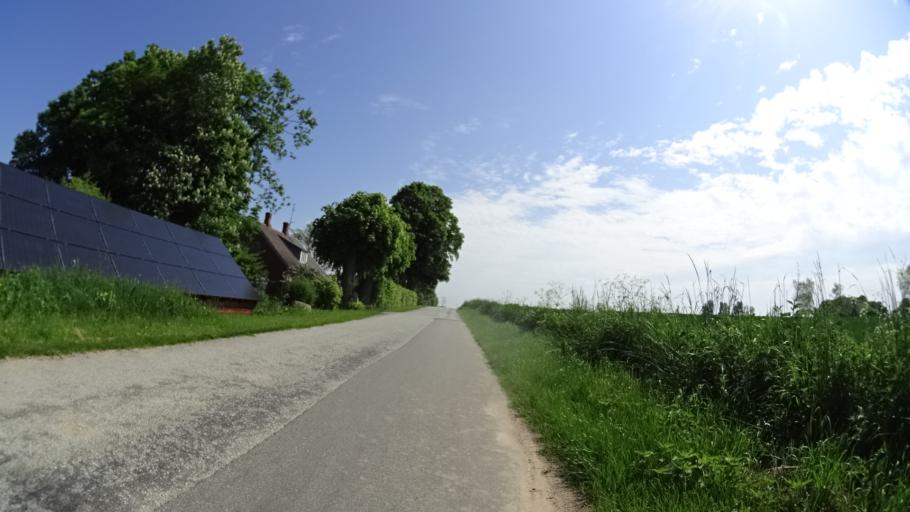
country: DK
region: Central Jutland
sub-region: Skanderborg Kommune
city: Horning
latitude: 56.1168
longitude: 10.0181
